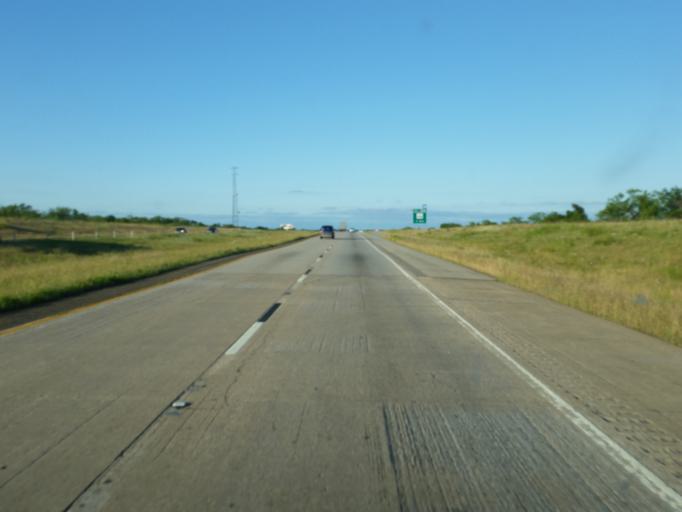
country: US
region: Texas
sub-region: Kaufman County
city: Talty
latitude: 32.7080
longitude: -96.3460
